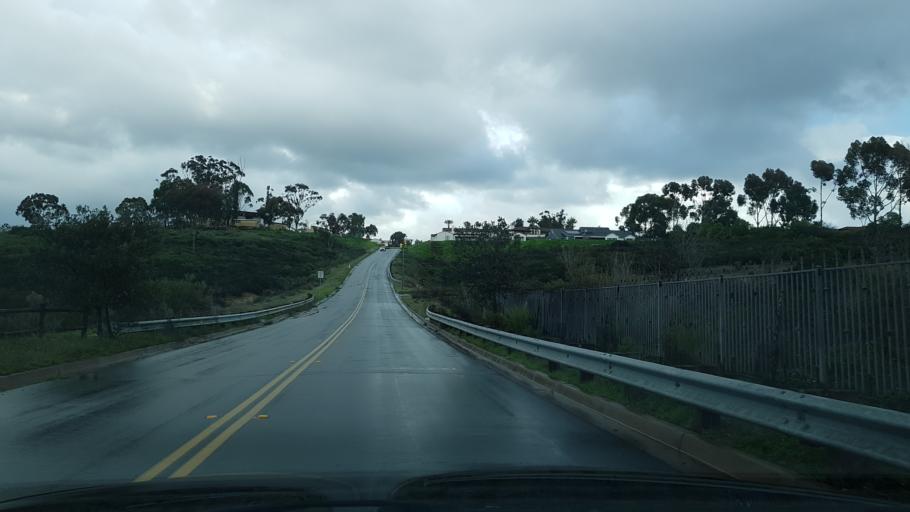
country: US
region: California
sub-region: San Diego County
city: Fairbanks Ranch
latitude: 32.9423
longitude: -117.1918
